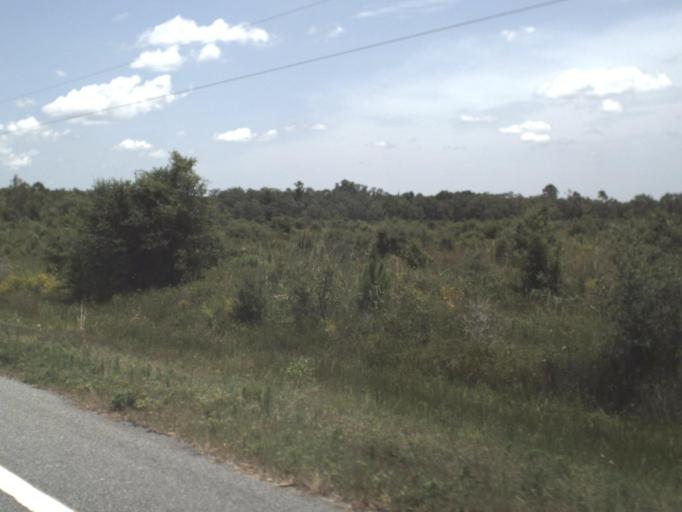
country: US
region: Florida
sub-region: Taylor County
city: Steinhatchee
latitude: 29.8046
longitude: -83.3189
